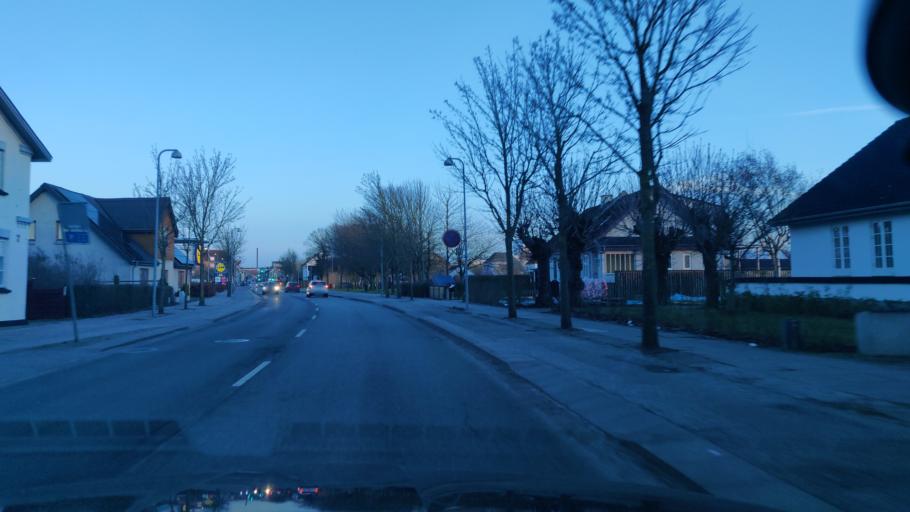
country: DK
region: North Denmark
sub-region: Alborg Kommune
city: Aalborg
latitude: 57.0639
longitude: 9.9078
